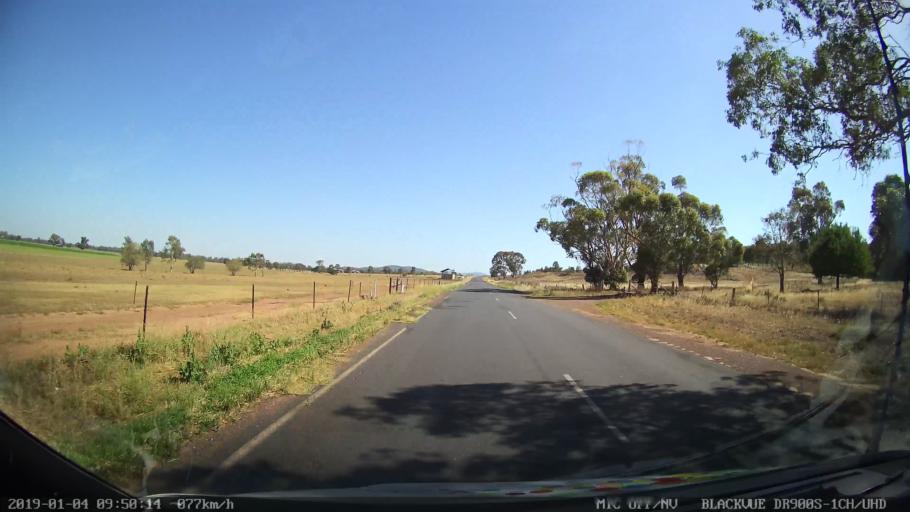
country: AU
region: New South Wales
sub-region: Cabonne
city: Canowindra
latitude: -33.5866
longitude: 148.4148
